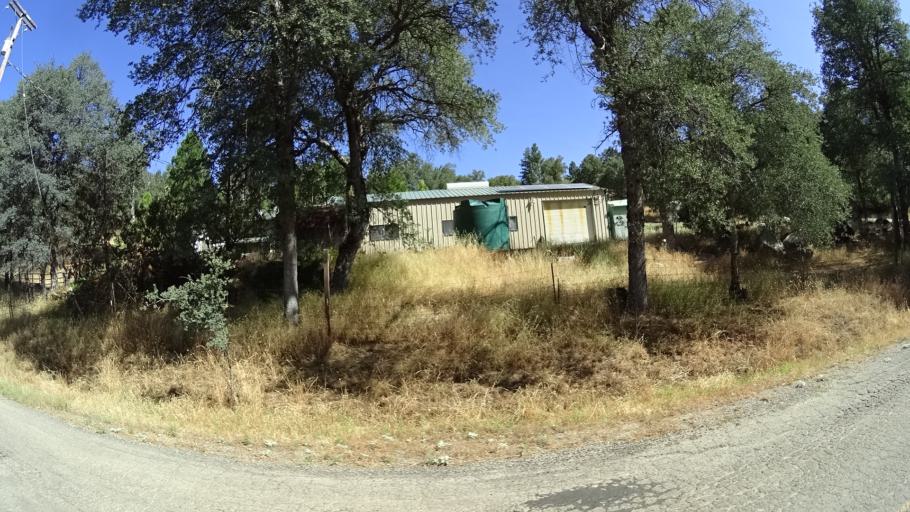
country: US
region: California
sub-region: Amador County
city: Pioneer
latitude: 38.3982
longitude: -120.4847
